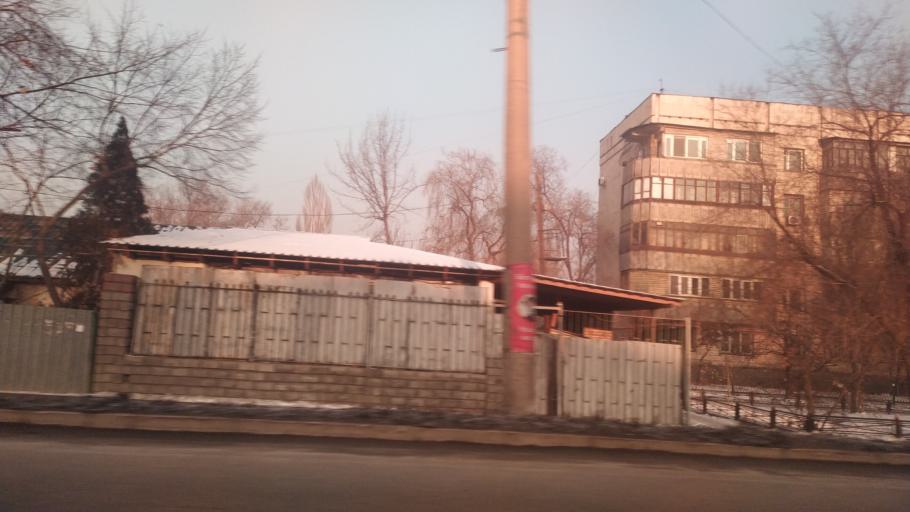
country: KZ
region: Almaty Qalasy
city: Almaty
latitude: 43.2543
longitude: 76.8609
